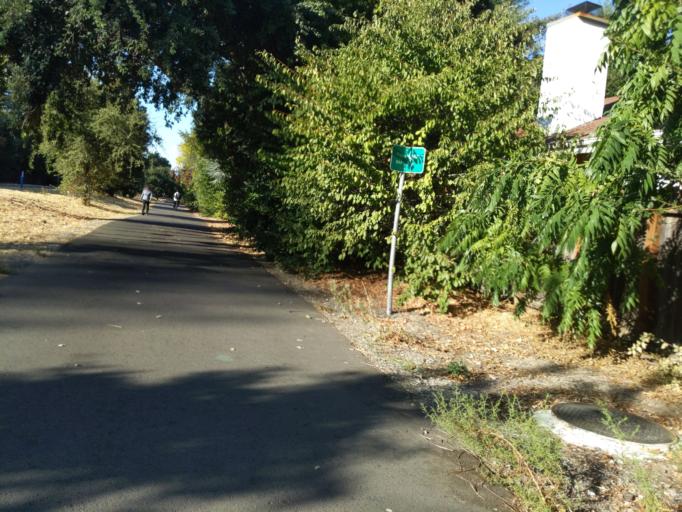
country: US
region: California
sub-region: Contra Costa County
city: Waldon
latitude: 37.9229
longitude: -122.0552
